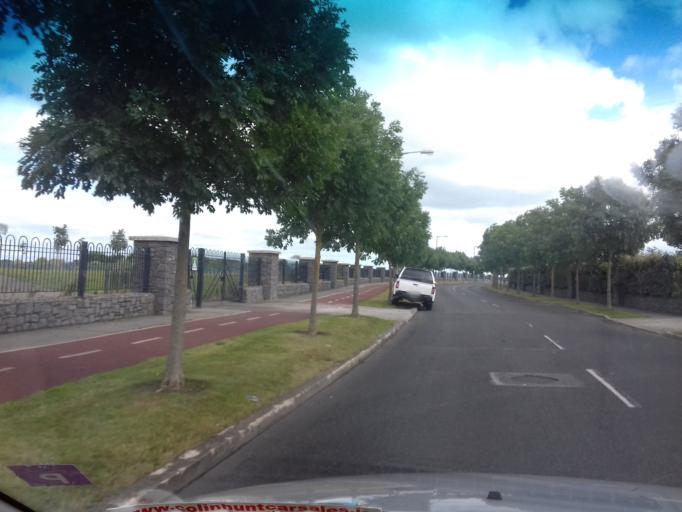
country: IE
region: Leinster
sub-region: Fingal County
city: Baldoyle
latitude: 53.4007
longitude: -6.1353
